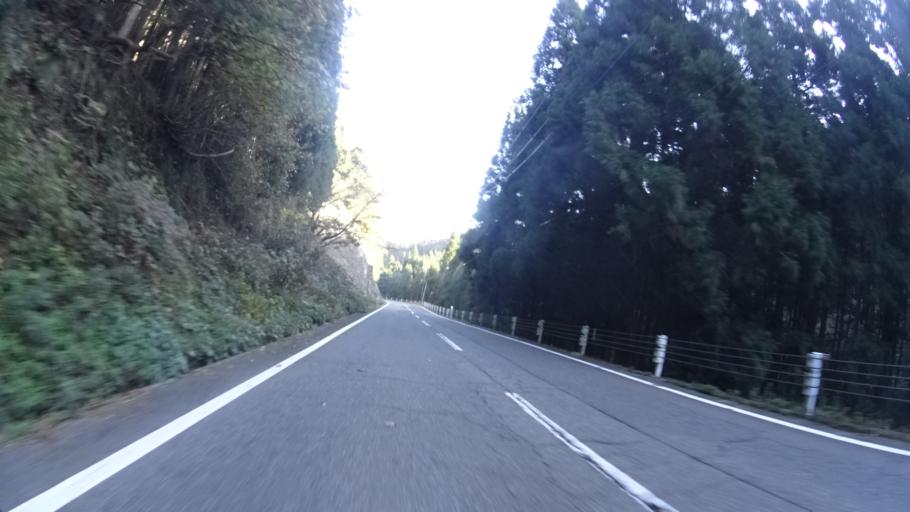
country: JP
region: Fukui
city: Maruoka
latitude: 36.1399
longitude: 136.3251
